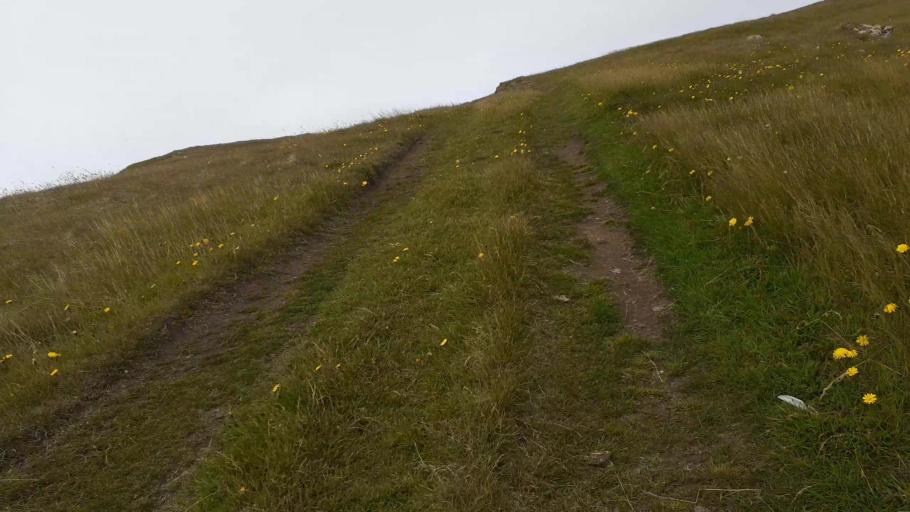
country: IS
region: Northeast
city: Dalvik
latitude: 66.5343
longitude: -17.9831
